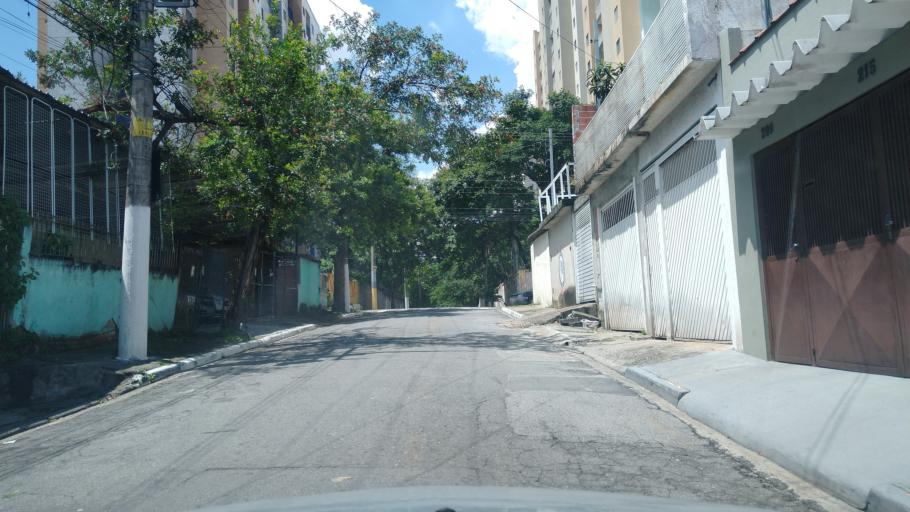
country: BR
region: Sao Paulo
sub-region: Sao Paulo
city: Sao Paulo
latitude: -23.4695
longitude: -46.6689
